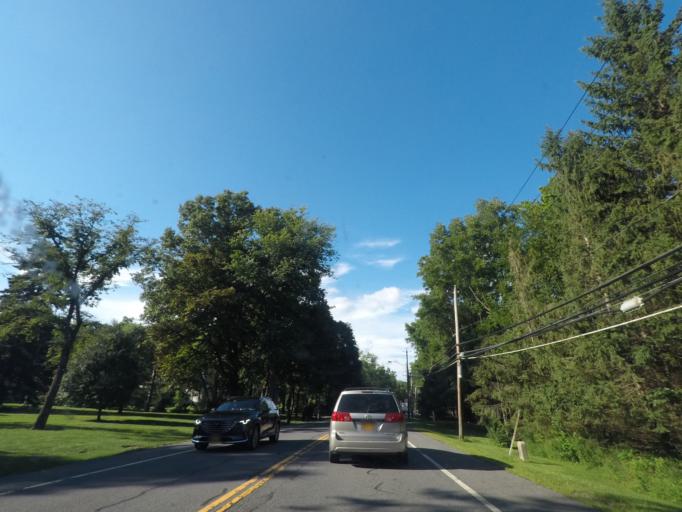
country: US
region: New York
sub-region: Albany County
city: West Albany
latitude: 42.6907
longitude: -73.7529
